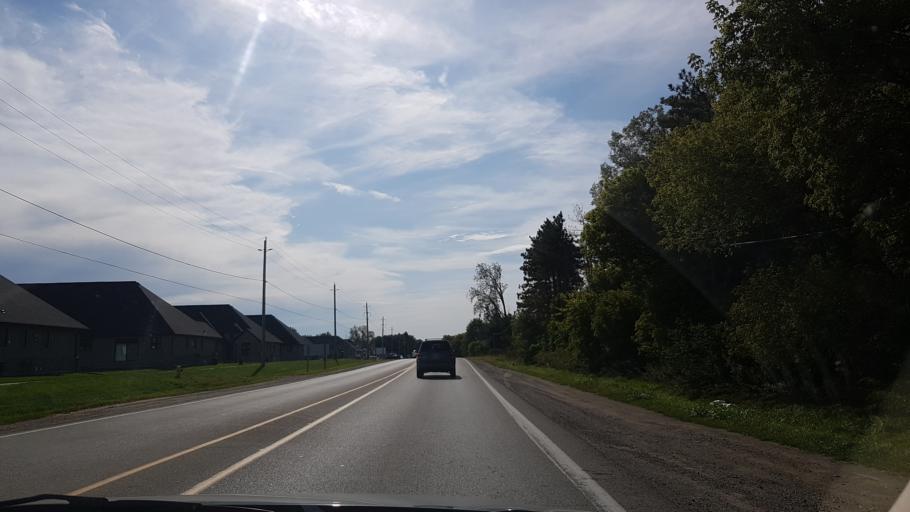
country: CA
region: Ontario
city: Delaware
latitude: 42.9436
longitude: -81.4331
